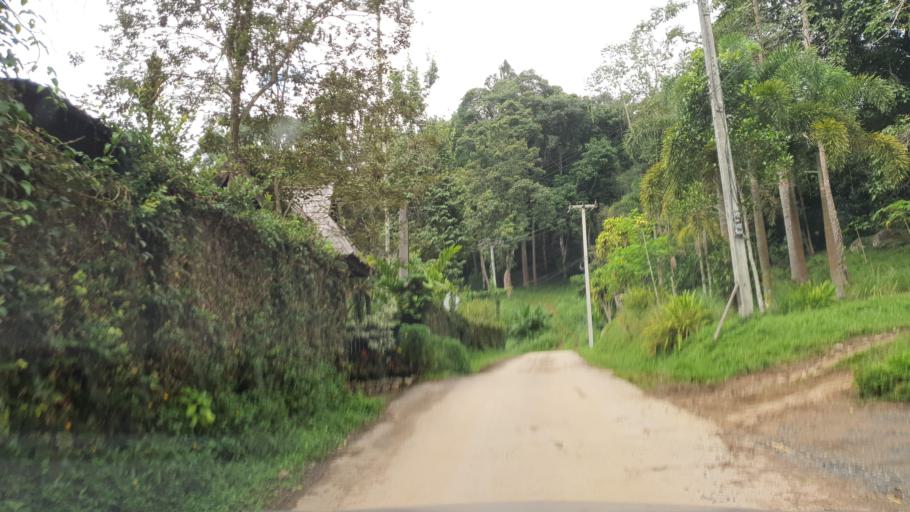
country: TH
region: Chiang Mai
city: Mae On
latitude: 18.9250
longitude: 99.3123
